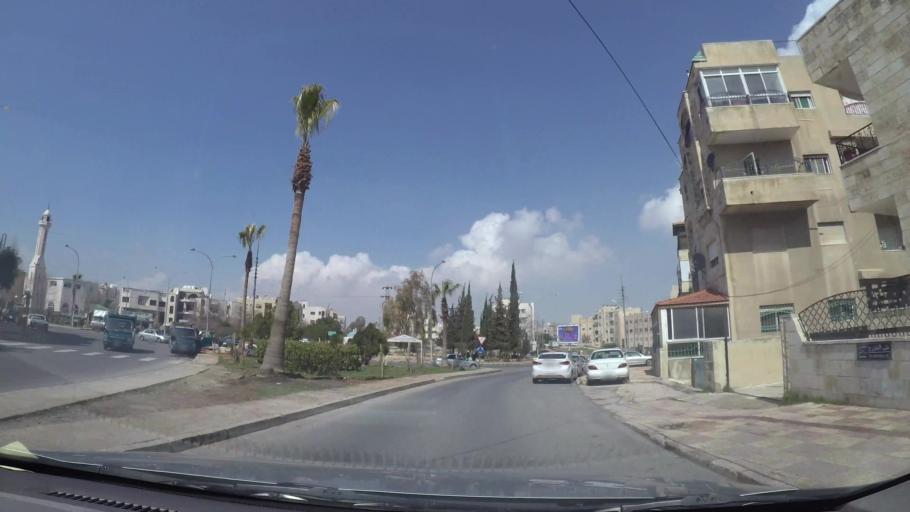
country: JO
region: Amman
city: Al Bunayyat ash Shamaliyah
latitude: 31.9293
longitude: 35.9044
